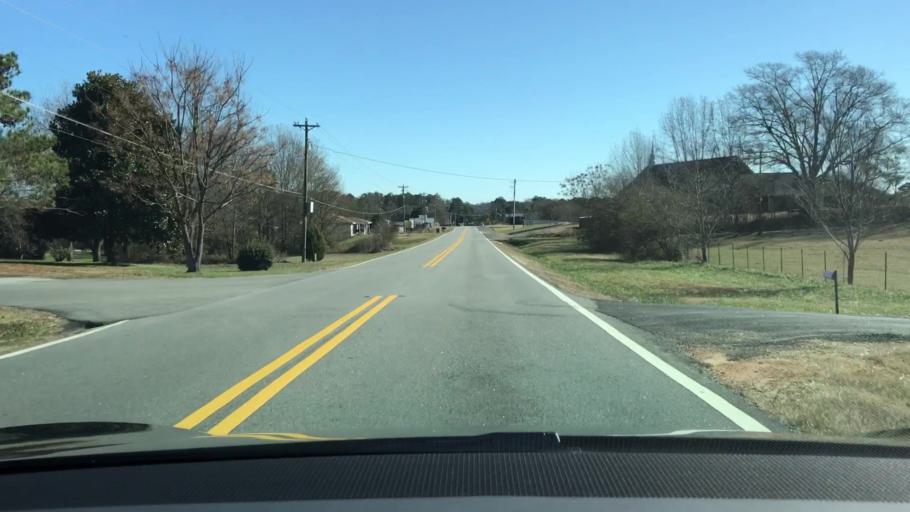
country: US
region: Georgia
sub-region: Barrow County
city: Auburn
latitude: 33.9027
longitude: -83.8073
